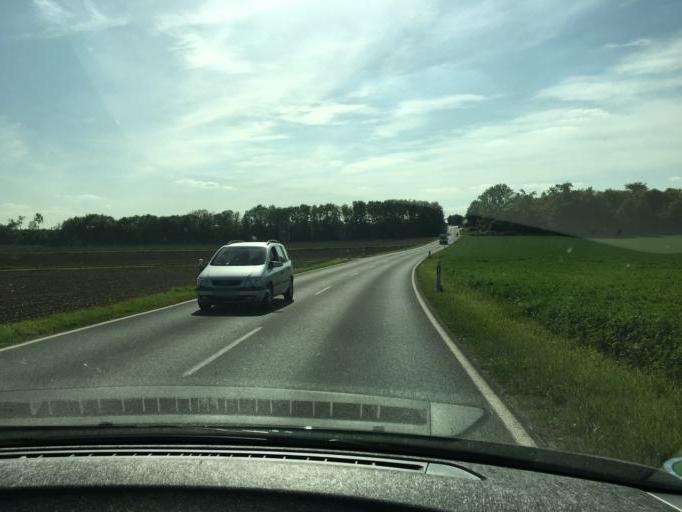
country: DE
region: North Rhine-Westphalia
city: Wesseling
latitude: 50.7931
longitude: 6.9715
